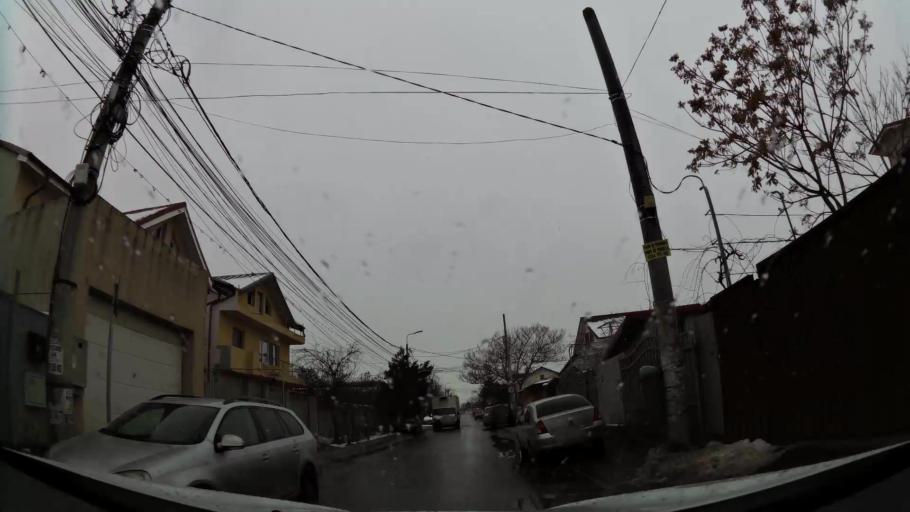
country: RO
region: Ilfov
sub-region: Comuna Chiajna
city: Rosu
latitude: 44.4085
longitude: 26.0111
